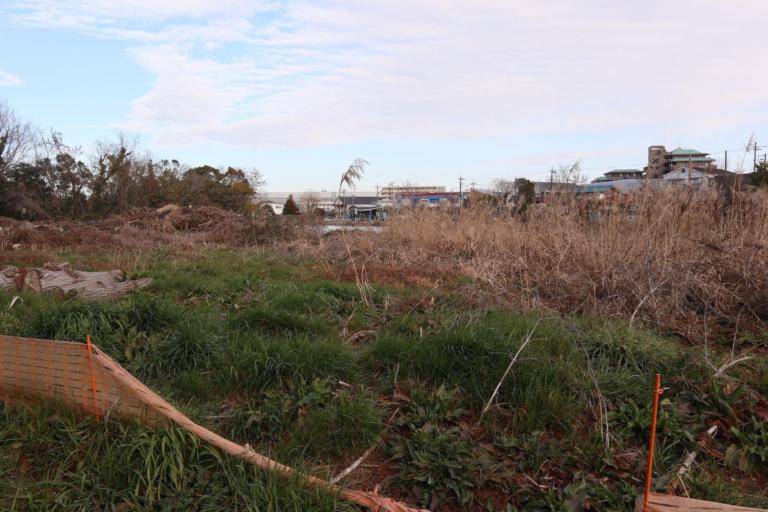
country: JP
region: Chiba
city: Matsudo
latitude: 35.7918
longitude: 139.8742
